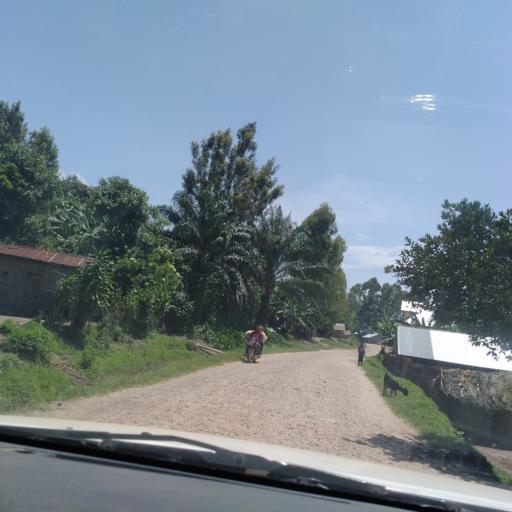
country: RW
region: Western Province
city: Kibuye
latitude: -2.0052
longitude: 28.9108
